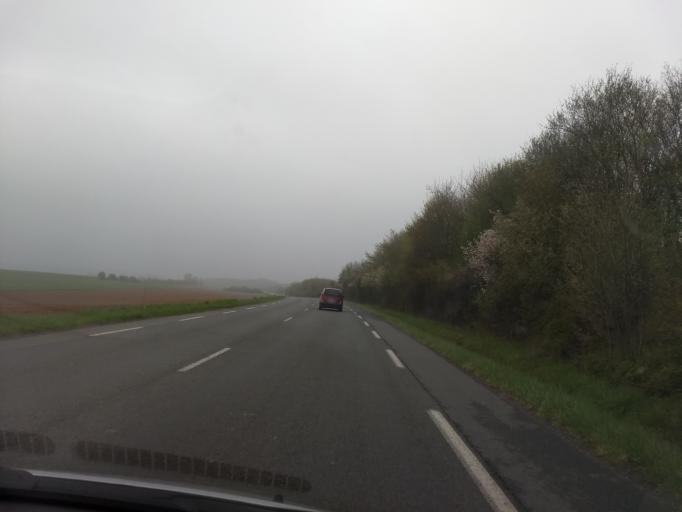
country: FR
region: Nord-Pas-de-Calais
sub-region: Departement du Pas-de-Calais
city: Montreuil
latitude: 50.4269
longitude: 1.7224
